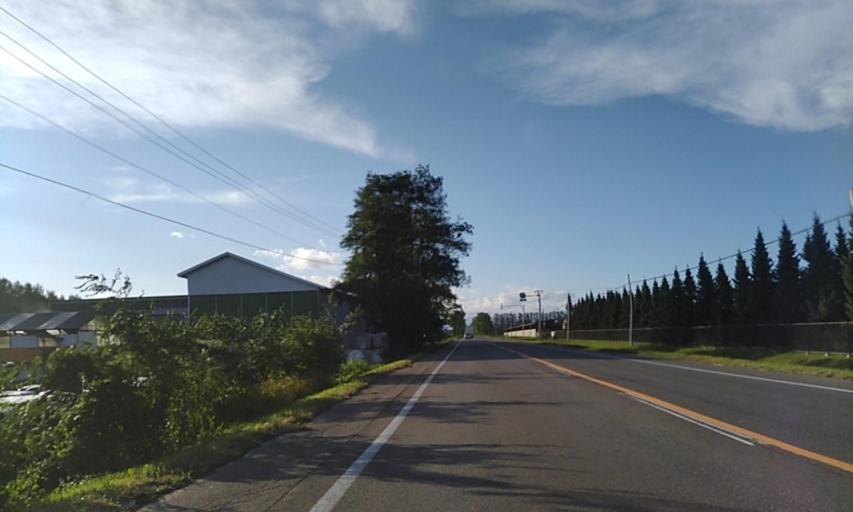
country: JP
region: Hokkaido
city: Obihiro
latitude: 42.9195
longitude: 142.9975
